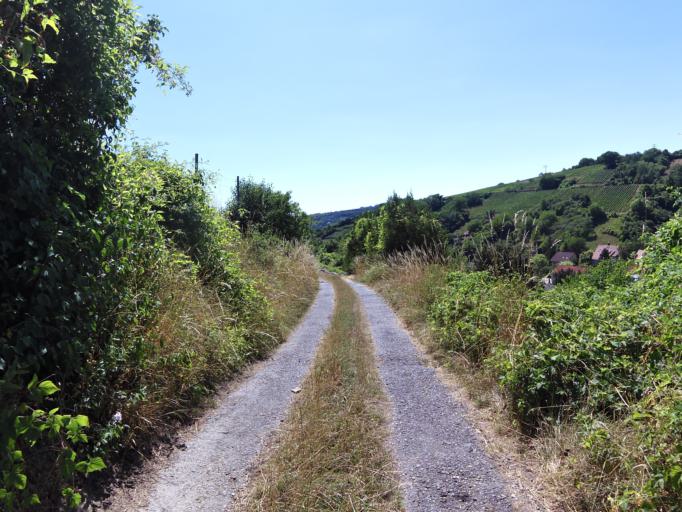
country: DE
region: Bavaria
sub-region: Regierungsbezirk Unterfranken
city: Gerbrunn
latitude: 49.7663
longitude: 9.9935
